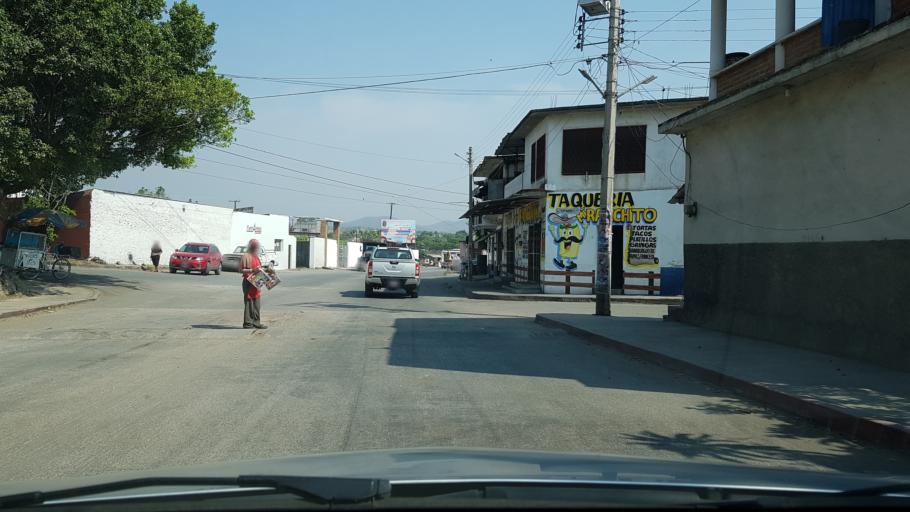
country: MX
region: Morelos
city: Zacatepec
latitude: 18.6642
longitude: -99.1860
